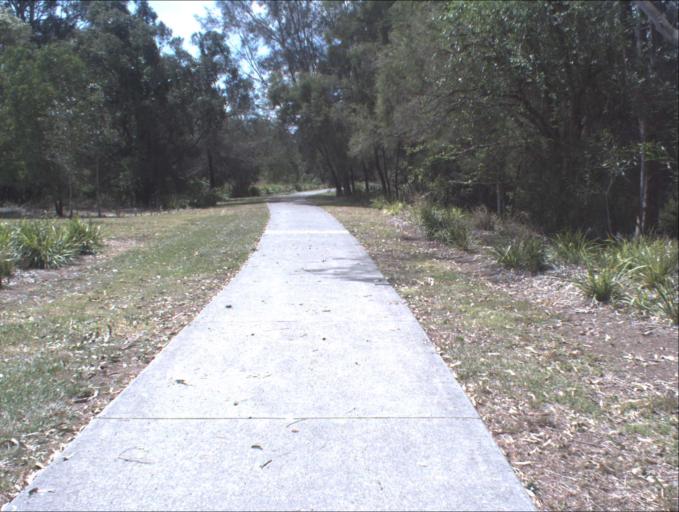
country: AU
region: Queensland
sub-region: Logan
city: Slacks Creek
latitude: -27.6702
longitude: 153.1596
